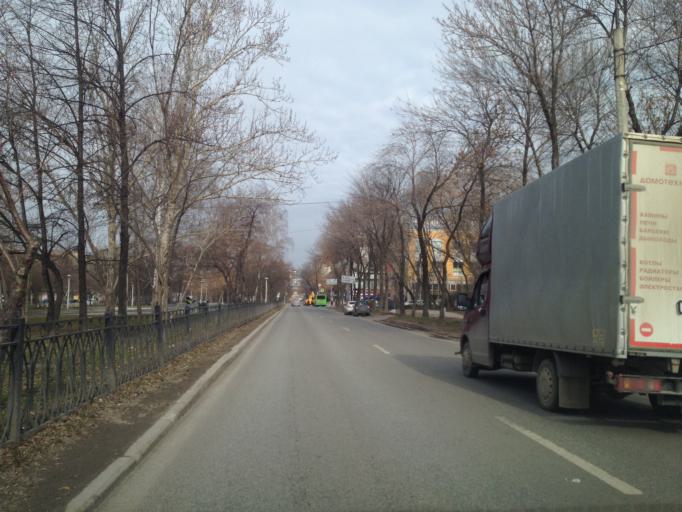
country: RU
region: Sverdlovsk
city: Yekaterinburg
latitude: 56.8201
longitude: 60.5787
